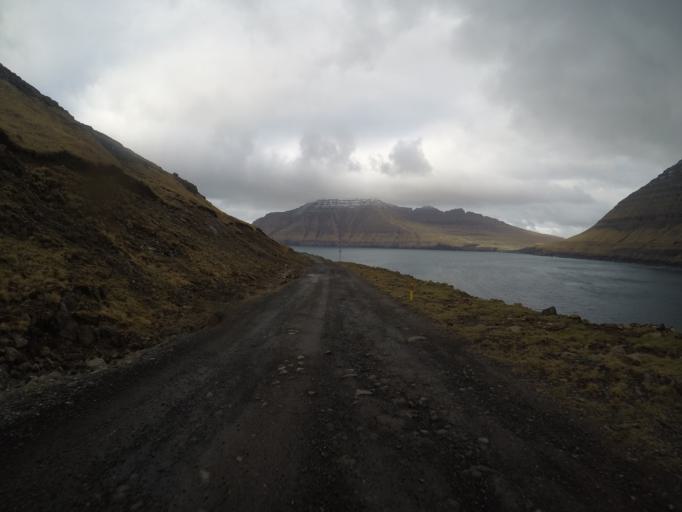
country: FO
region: Nordoyar
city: Klaksvik
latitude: 62.3421
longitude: -6.5806
